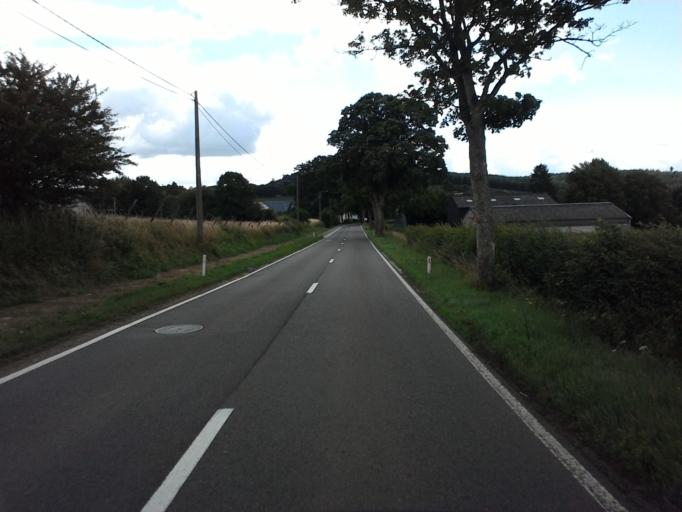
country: BE
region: Wallonia
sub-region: Province du Luxembourg
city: Leglise
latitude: 49.8029
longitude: 5.5304
